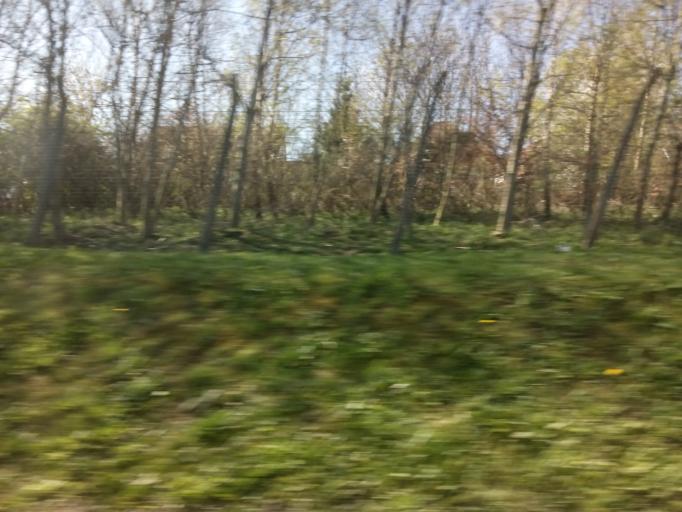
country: GB
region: Scotland
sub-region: Edinburgh
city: Currie
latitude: 55.9366
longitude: -3.3001
